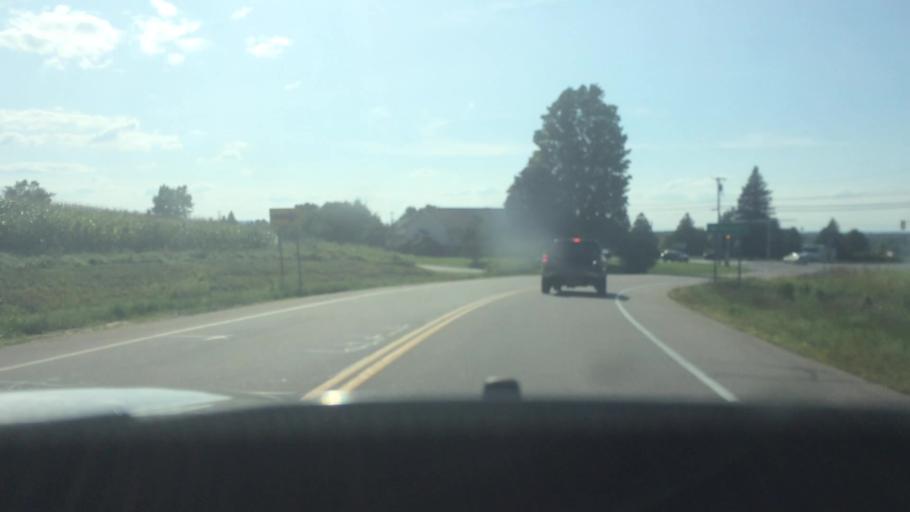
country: US
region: New York
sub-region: Franklin County
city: Malone
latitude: 44.8585
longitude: -74.2563
